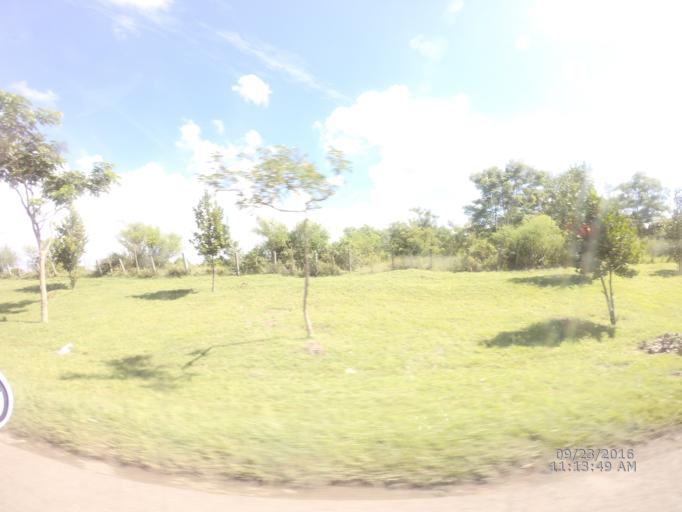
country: CU
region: La Habana
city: Arroyo Naranjo
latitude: 23.0319
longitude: -82.3004
